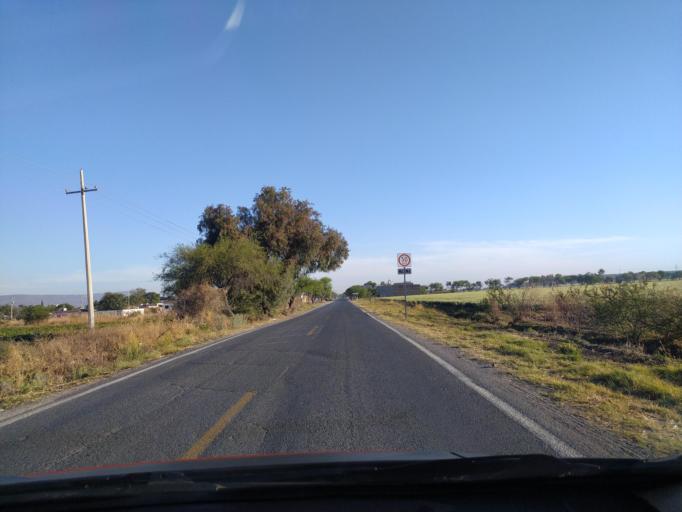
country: MX
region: Guanajuato
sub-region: San Francisco del Rincon
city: San Ignacio de Hidalgo
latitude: 20.9072
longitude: -101.8577
